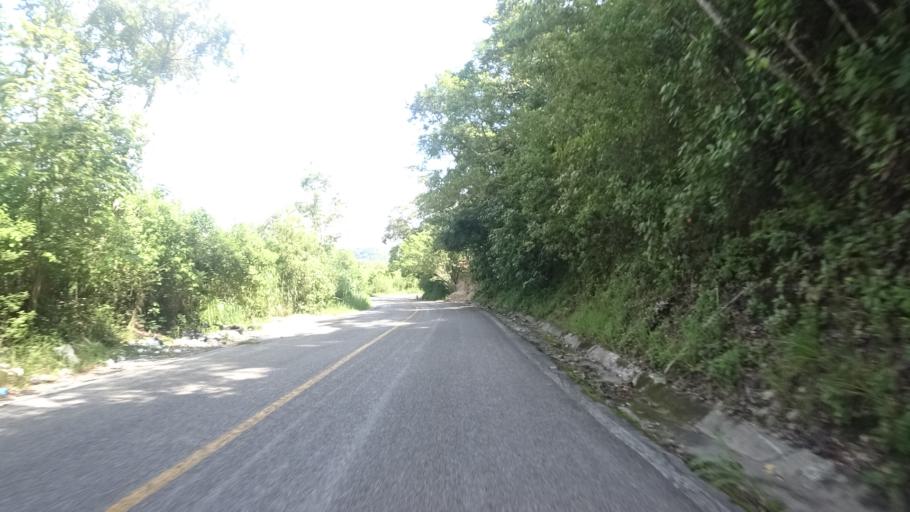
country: MX
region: Chiapas
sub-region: Palenque
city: Doctor Samuel Leon Brindis
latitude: 17.4437
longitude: -91.9687
